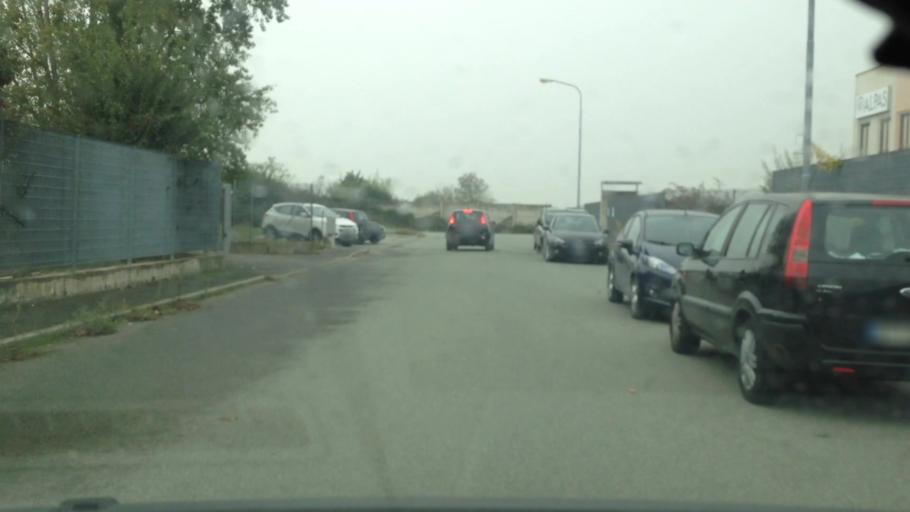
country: IT
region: Piedmont
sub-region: Provincia di Alessandria
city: Solero
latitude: 44.9160
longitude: 8.4818
